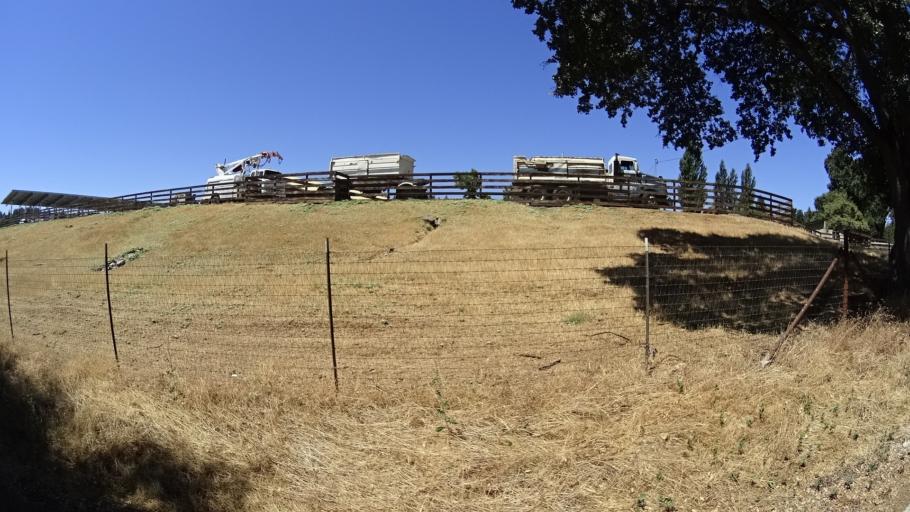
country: US
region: California
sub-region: Calaveras County
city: Mountain Ranch
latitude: 38.2208
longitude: -120.5444
